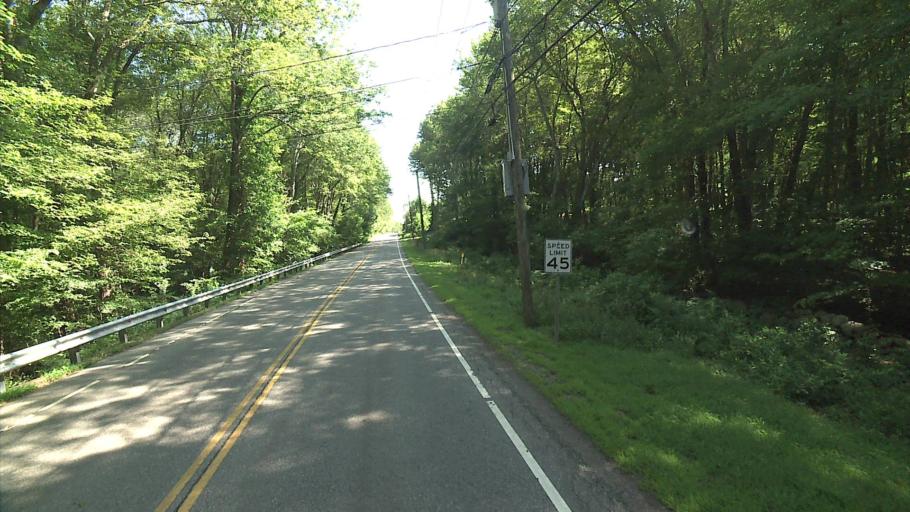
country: US
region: Connecticut
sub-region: New London County
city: Montville Center
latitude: 41.5282
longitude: -72.2063
